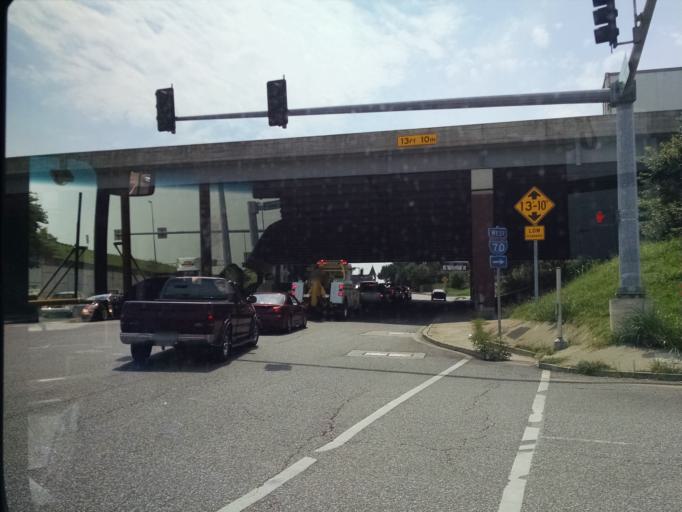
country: US
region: Illinois
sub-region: Madison County
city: Venice
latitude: 38.6734
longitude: -90.2038
